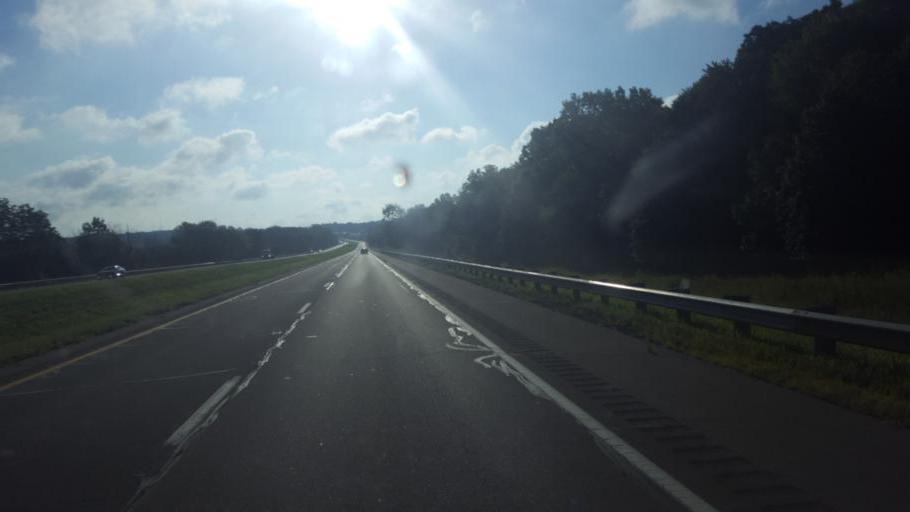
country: US
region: Ohio
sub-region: Wayne County
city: Shreve
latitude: 40.7842
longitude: -82.1168
